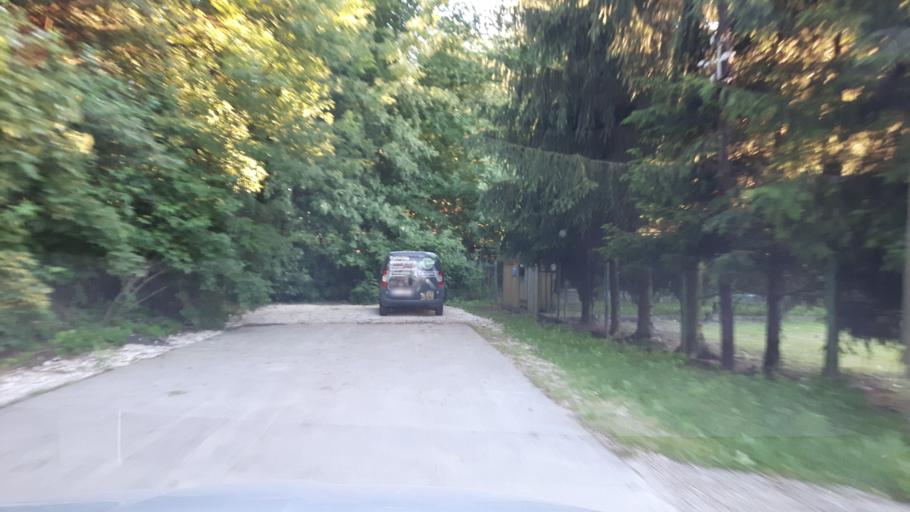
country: PL
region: Masovian Voivodeship
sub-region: Warszawa
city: Praga Poludnie
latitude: 52.2696
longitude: 21.0850
